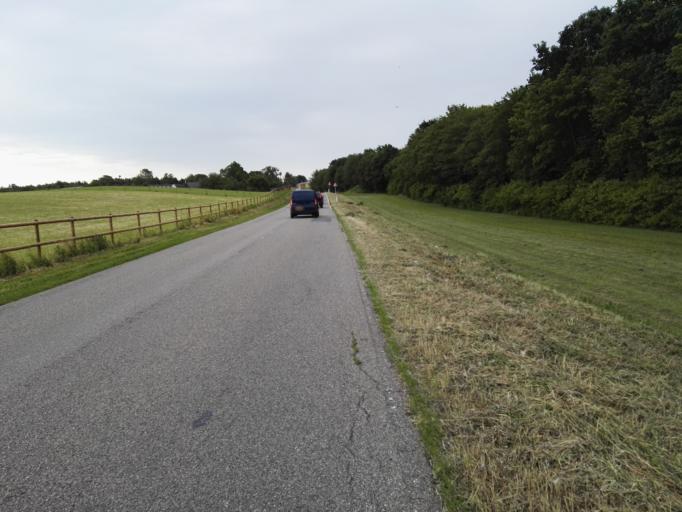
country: DK
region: Zealand
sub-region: Roskilde Kommune
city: Jyllinge
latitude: 55.7803
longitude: 12.1199
